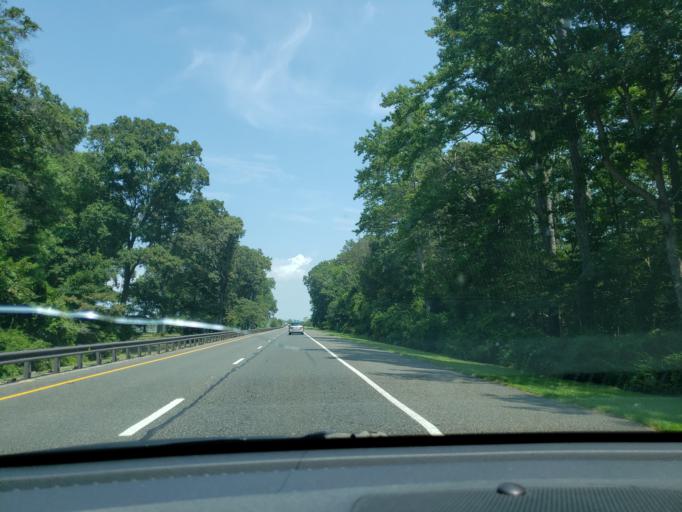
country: US
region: New Jersey
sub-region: Cape May County
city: Rio Grande
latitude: 38.9989
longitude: -74.8748
